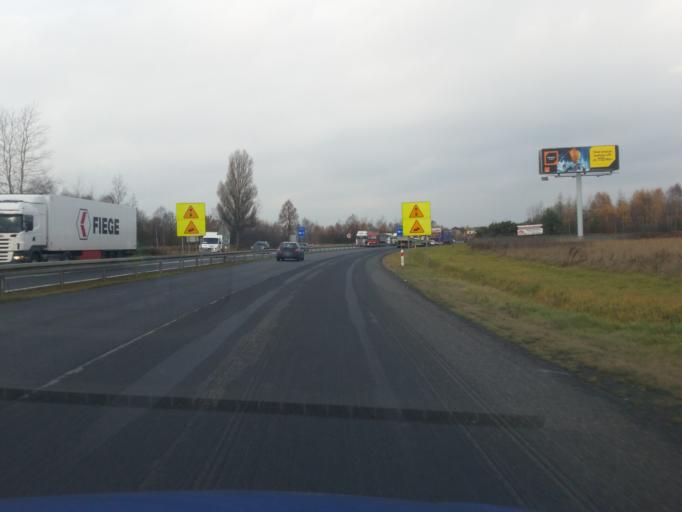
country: PL
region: Silesian Voivodeship
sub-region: Powiat myszkowski
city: Kozieglowy
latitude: 50.5938
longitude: 19.1521
